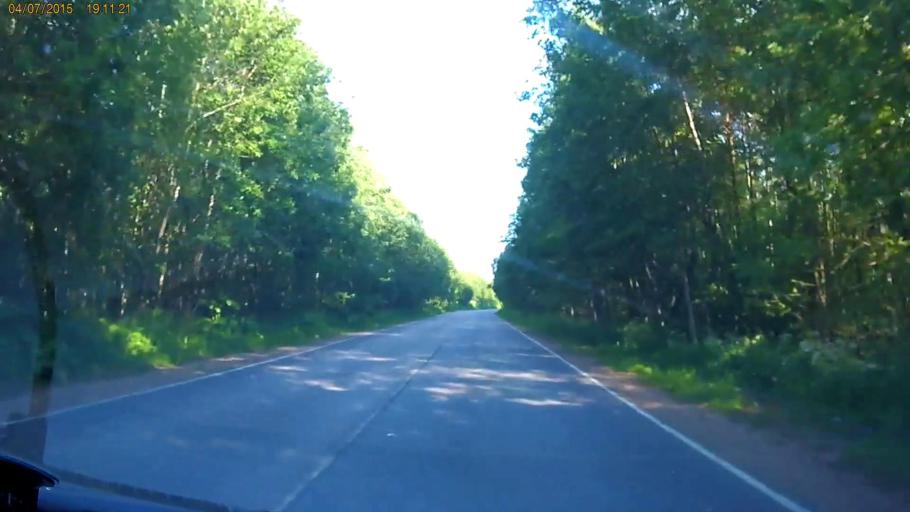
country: RU
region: Leningrad
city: Garbolovo
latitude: 60.3288
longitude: 30.4928
